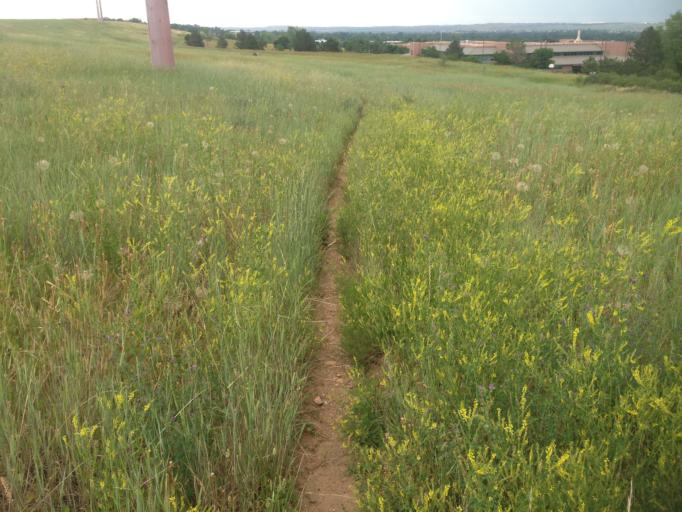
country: US
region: Colorado
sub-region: Boulder County
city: Superior
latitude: 39.9663
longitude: -105.1803
